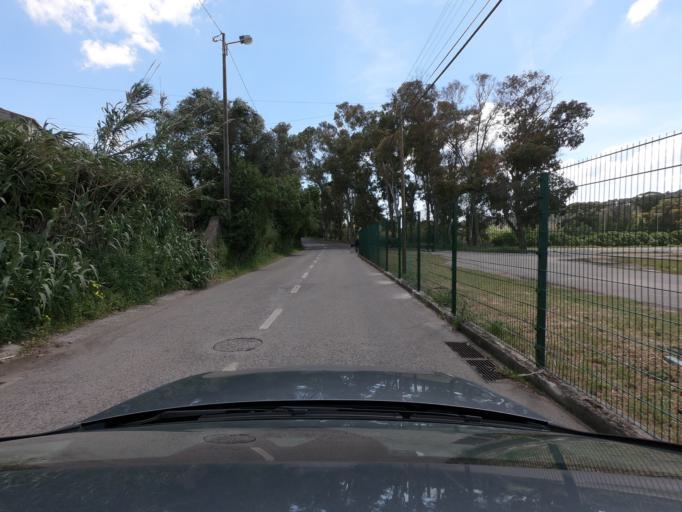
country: PT
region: Lisbon
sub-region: Oeiras
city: Linda-a-Velha
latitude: 38.7098
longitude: -9.2532
